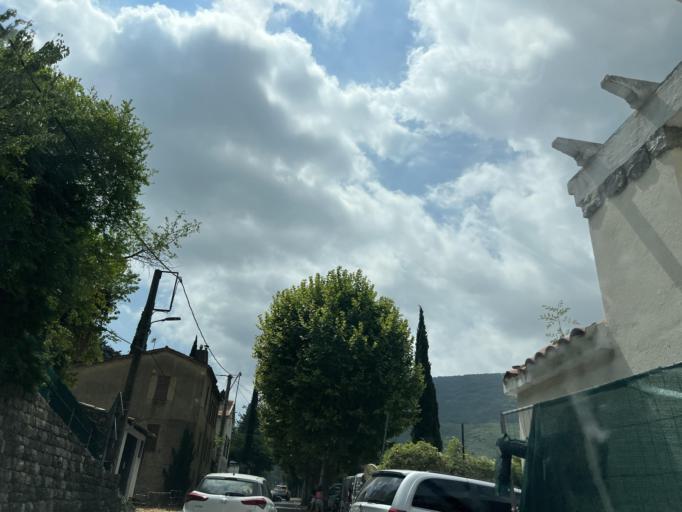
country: FR
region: Provence-Alpes-Cote d'Azur
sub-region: Departement des Alpes-Maritimes
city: Le Rouret
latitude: 43.7193
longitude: 6.9927
